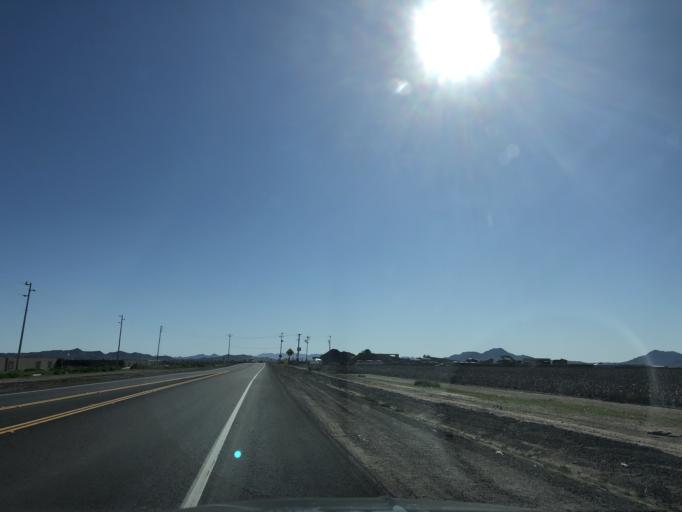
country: US
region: Arizona
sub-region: Maricopa County
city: Buckeye
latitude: 33.3761
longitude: -112.4778
